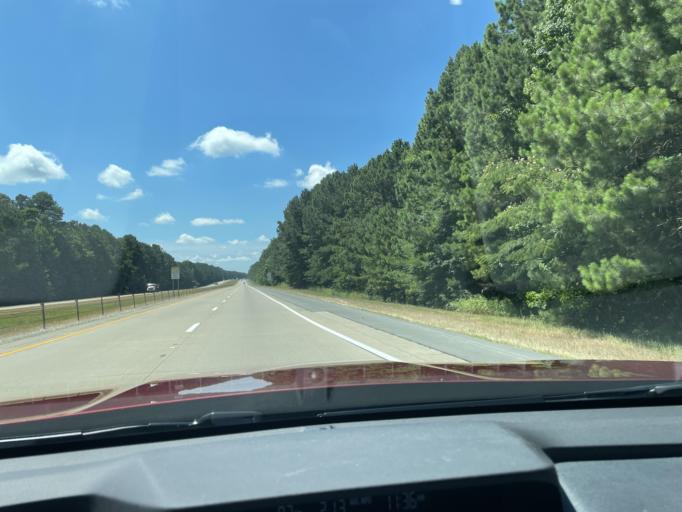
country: US
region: Arkansas
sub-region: Jefferson County
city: Redfield
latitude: 34.4345
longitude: -92.1952
